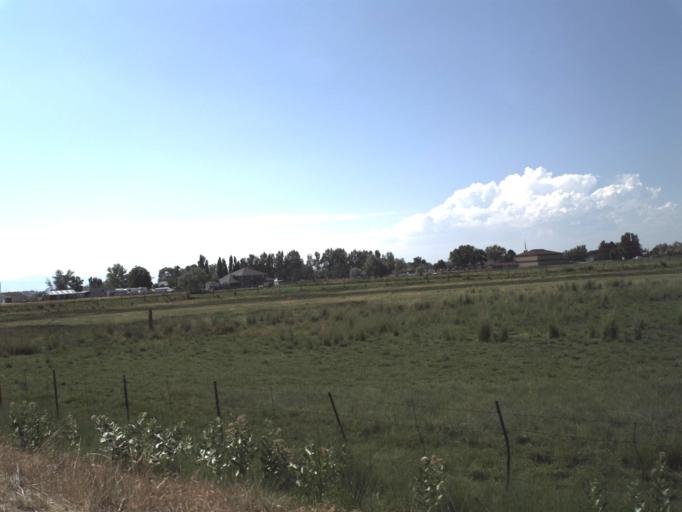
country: US
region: Utah
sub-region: Weber County
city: Marriott-Slaterville
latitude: 41.2444
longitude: -112.0696
